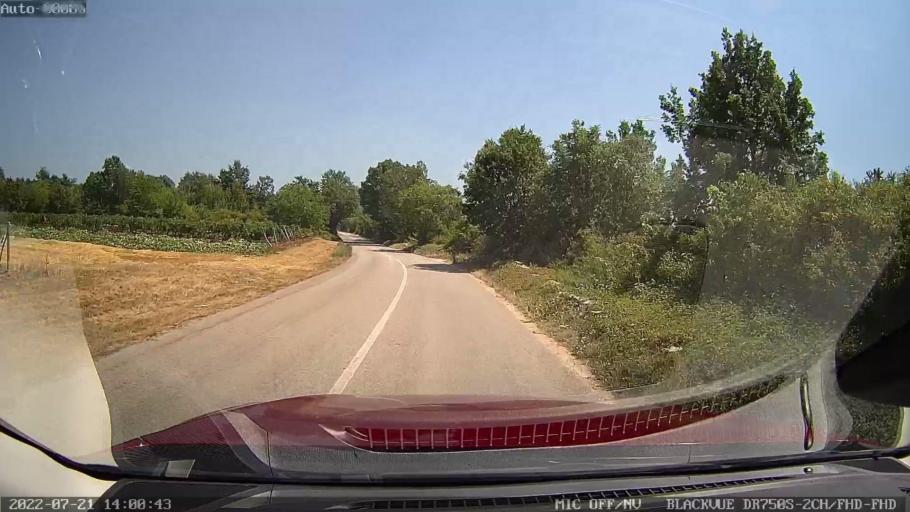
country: HR
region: Istarska
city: Vodnjan
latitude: 45.0966
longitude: 13.8722
